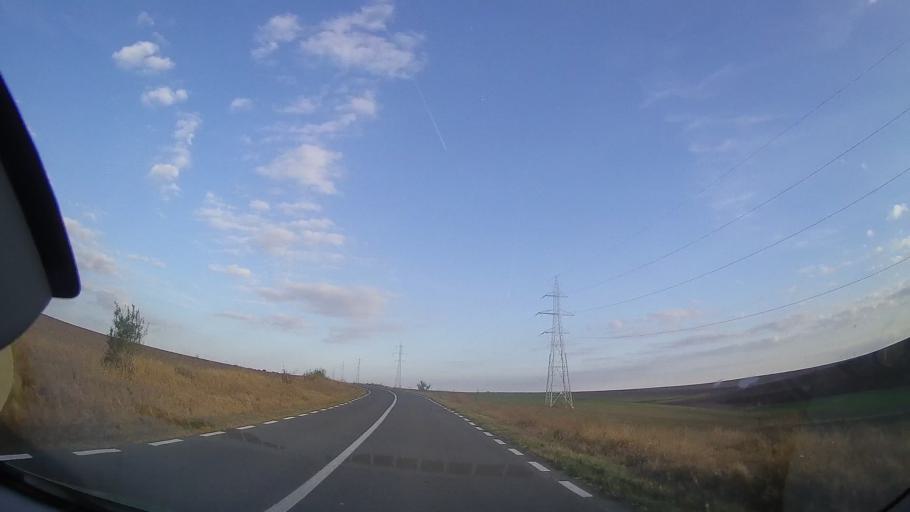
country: RO
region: Constanta
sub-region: Comuna Chirnogeni
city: Plopeni
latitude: 43.9525
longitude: 28.1571
